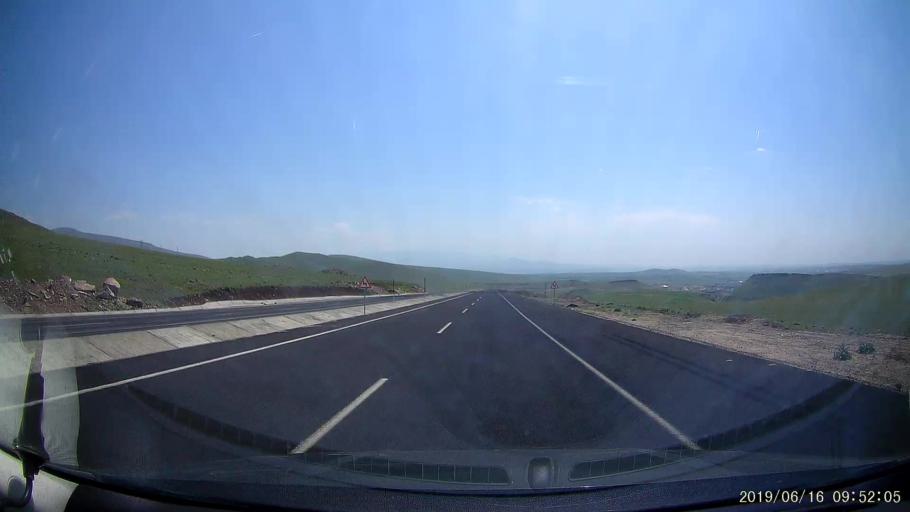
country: TR
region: Kars
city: Digor
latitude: 40.3924
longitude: 43.3792
